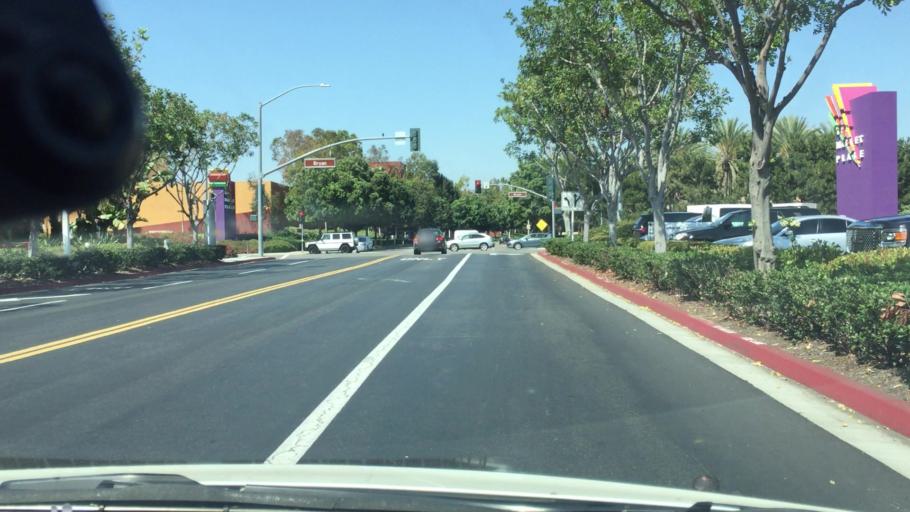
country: US
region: California
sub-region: Orange County
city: North Tustin
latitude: 33.7235
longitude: -117.7888
